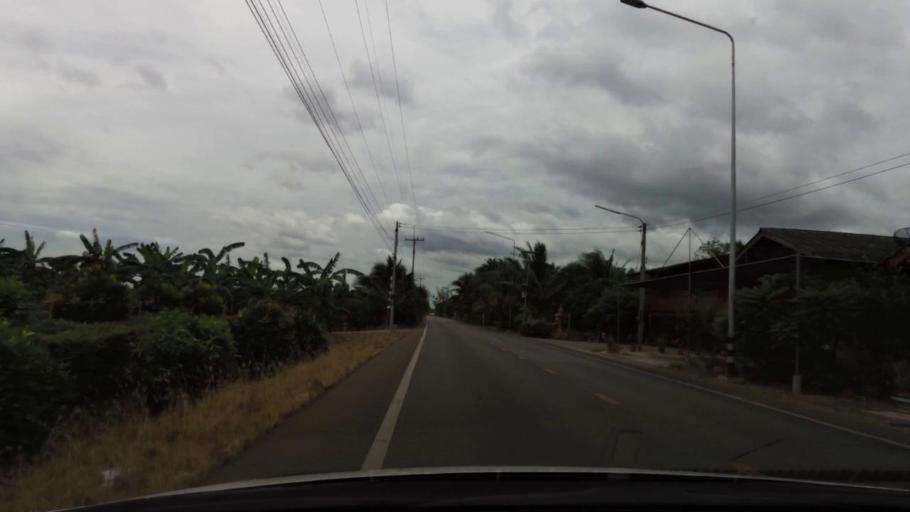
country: TH
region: Ratchaburi
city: Damnoen Saduak
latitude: 13.5638
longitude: 100.0126
